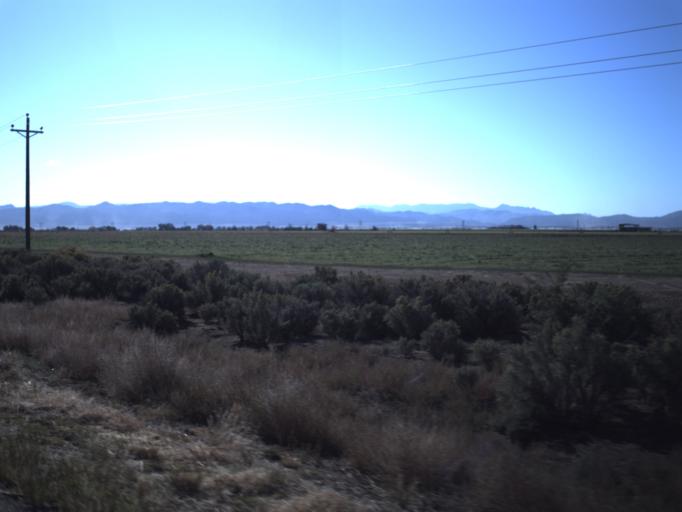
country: US
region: Utah
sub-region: Washington County
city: Enterprise
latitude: 37.7192
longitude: -113.6833
